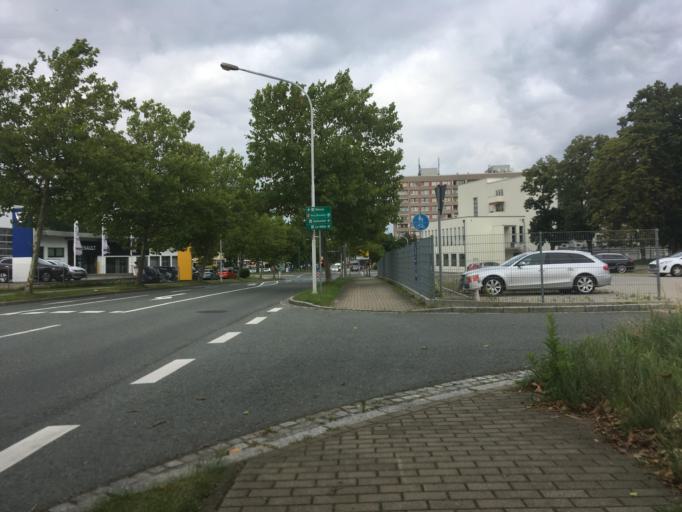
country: DE
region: Saxony
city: Riesa
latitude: 51.3049
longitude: 13.2907
